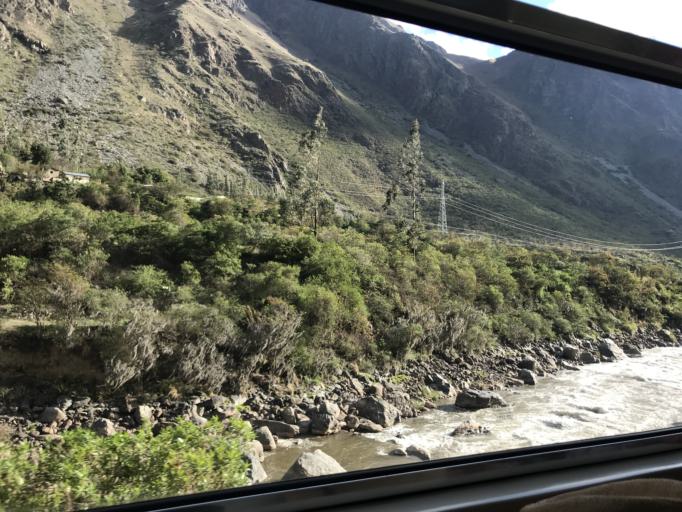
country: PE
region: Cusco
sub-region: Provincia de Urubamba
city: Ollantaytambo
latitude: -13.2270
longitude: -72.4030
